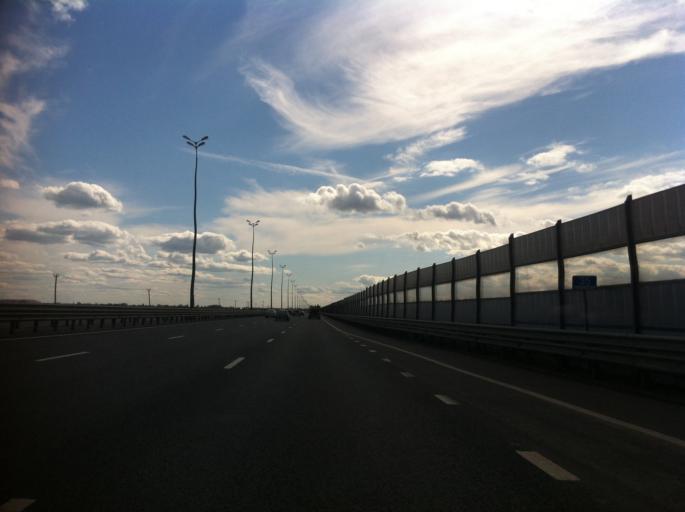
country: RU
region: Leningrad
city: Maloye Verevo
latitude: 59.6426
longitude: 30.2223
